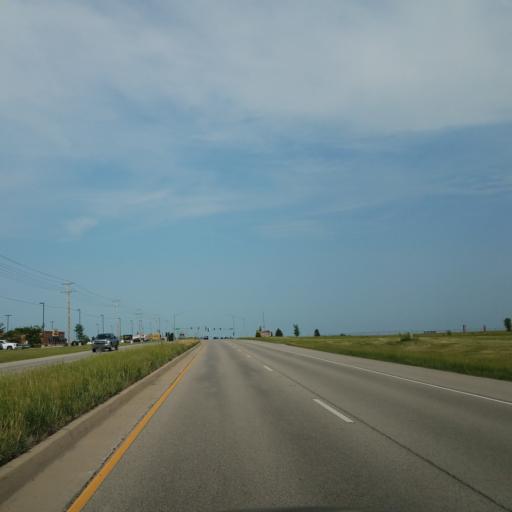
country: US
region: Illinois
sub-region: McLean County
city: Bloomington
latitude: 40.4882
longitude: -88.9133
